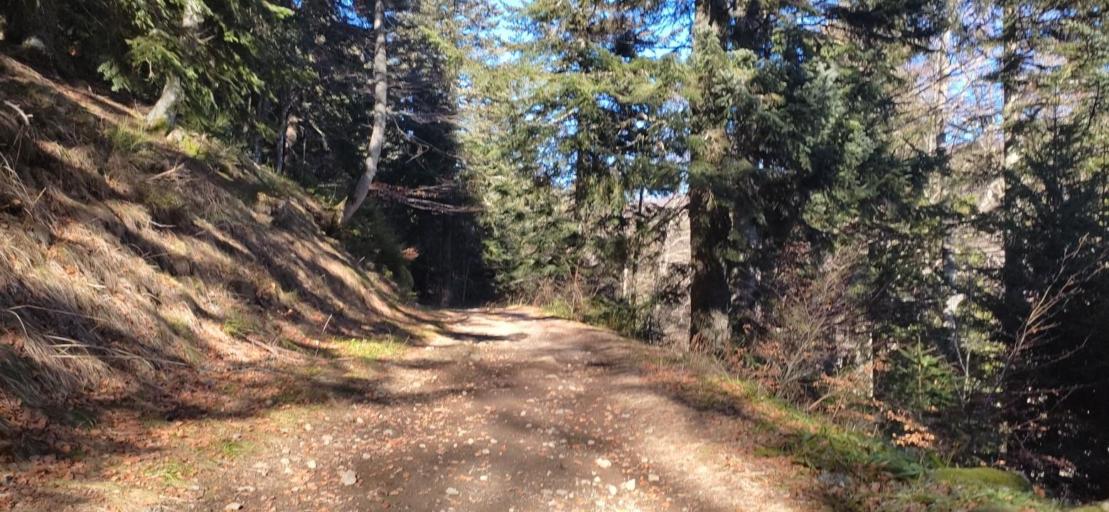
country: FR
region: Auvergne
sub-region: Departement du Puy-de-Dome
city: Mont-Dore
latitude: 45.5652
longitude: 2.8083
